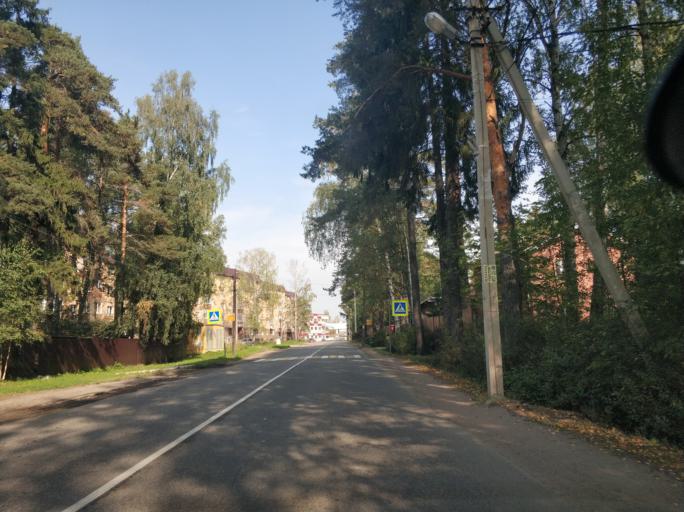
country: RU
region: Leningrad
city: Vsevolozhsk
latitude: 60.0150
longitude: 30.6226
